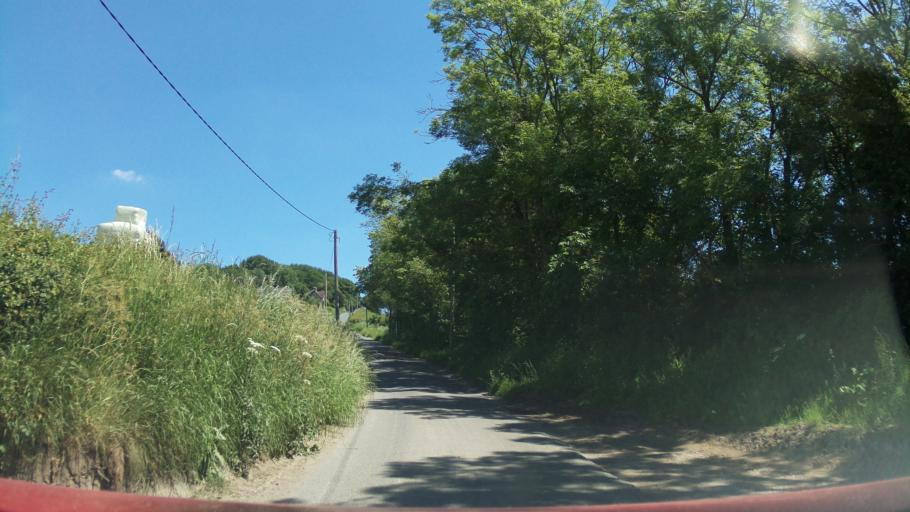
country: GB
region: England
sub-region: Wiltshire
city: Bremhill
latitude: 51.4556
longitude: -2.0594
